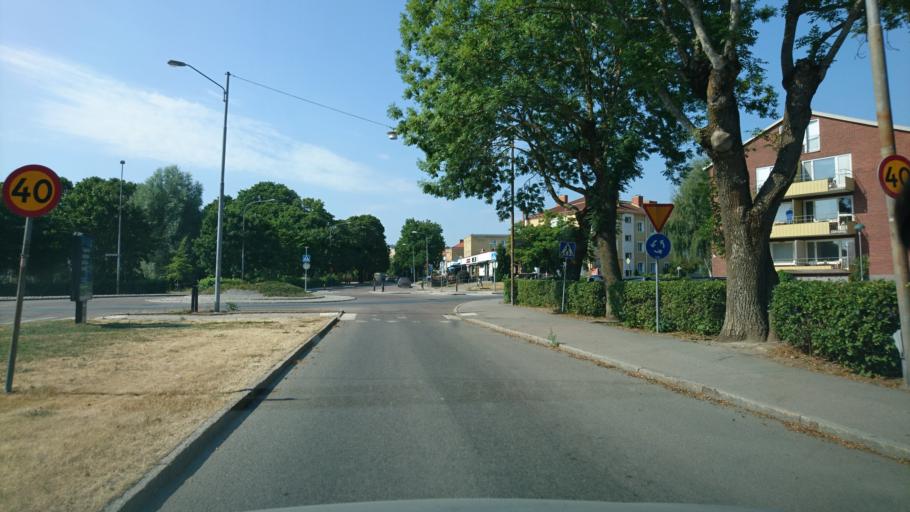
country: SE
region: Uppsala
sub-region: Uppsala Kommun
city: Uppsala
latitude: 59.8632
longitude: 17.6148
